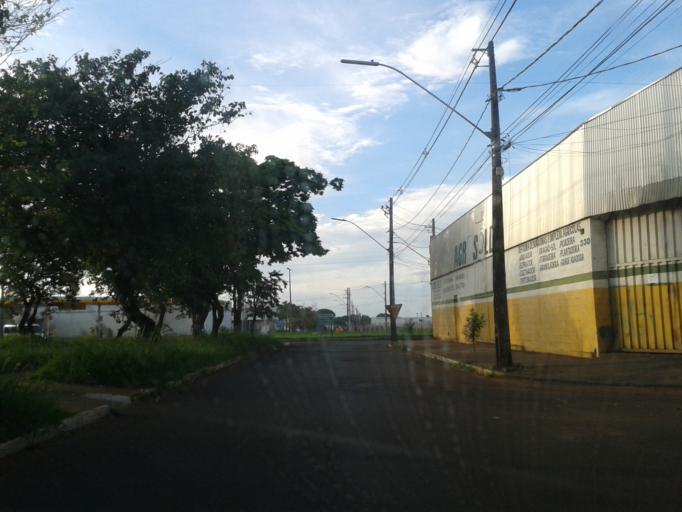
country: BR
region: Minas Gerais
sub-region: Araguari
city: Araguari
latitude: -18.6423
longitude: -48.2107
